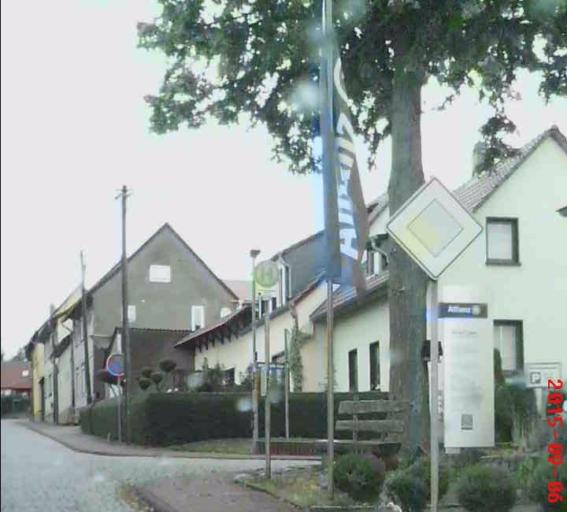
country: DE
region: Thuringia
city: Sollstedt
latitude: 51.2904
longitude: 10.4460
